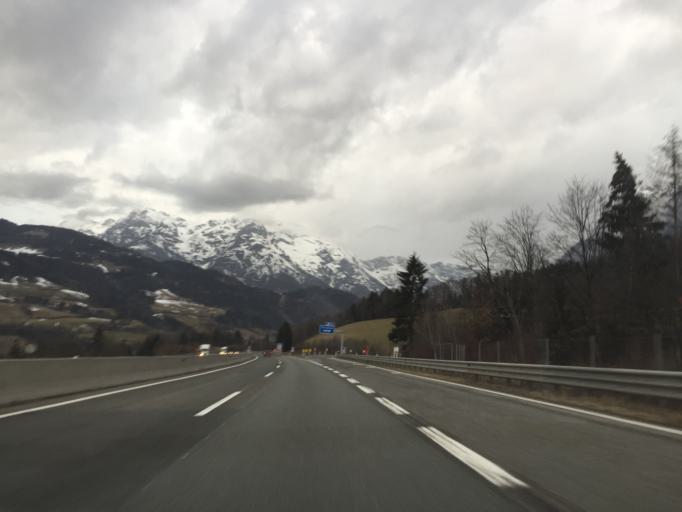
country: AT
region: Salzburg
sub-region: Politischer Bezirk Sankt Johann im Pongau
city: Pfarrwerfen
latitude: 47.4572
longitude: 13.2126
